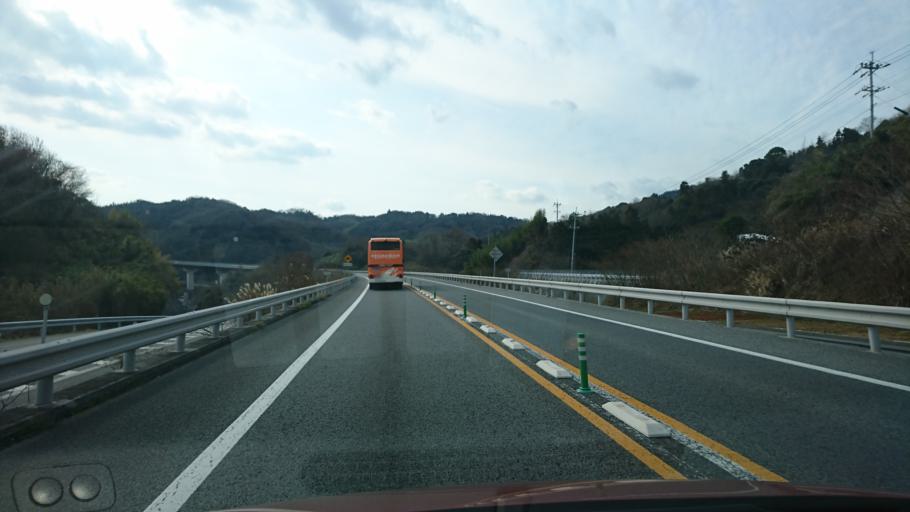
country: JP
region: Hiroshima
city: Innoshima
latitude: 34.1707
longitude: 133.0655
